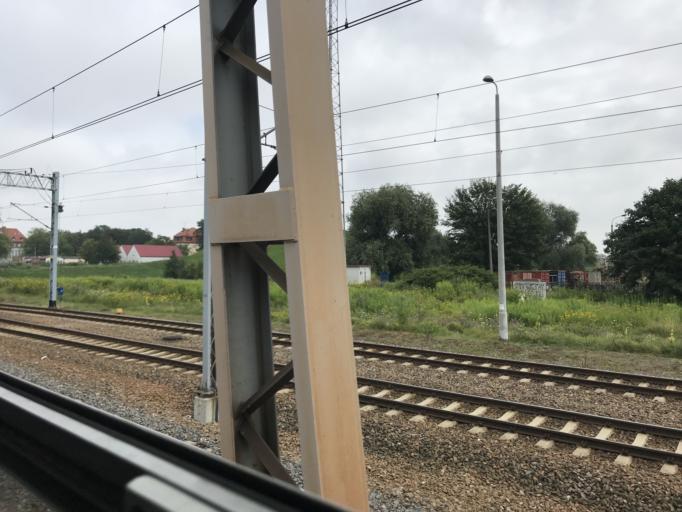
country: PL
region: Pomeranian Voivodeship
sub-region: Gdansk
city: Gdansk
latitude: 54.3398
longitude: 18.6423
